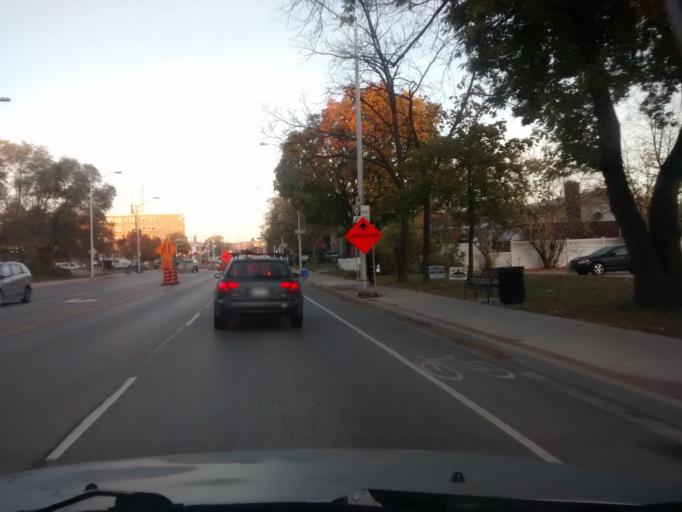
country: CA
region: Ontario
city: Burlington
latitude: 43.3332
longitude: -79.8088
